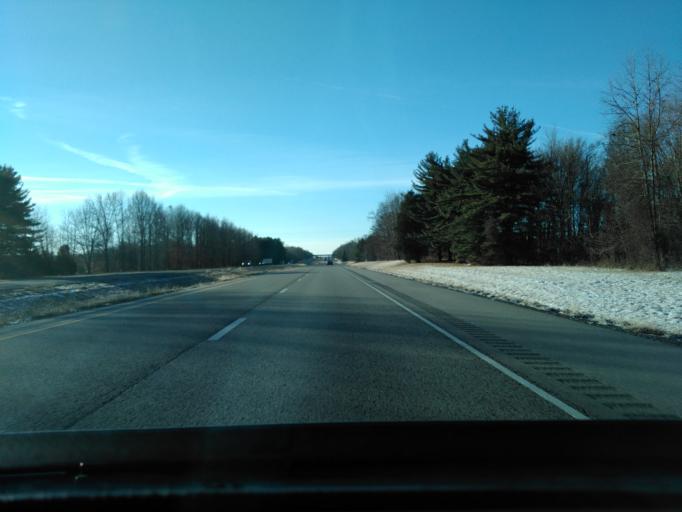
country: US
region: Illinois
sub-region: Franklin County
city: Benton
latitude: 37.9735
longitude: -88.9356
